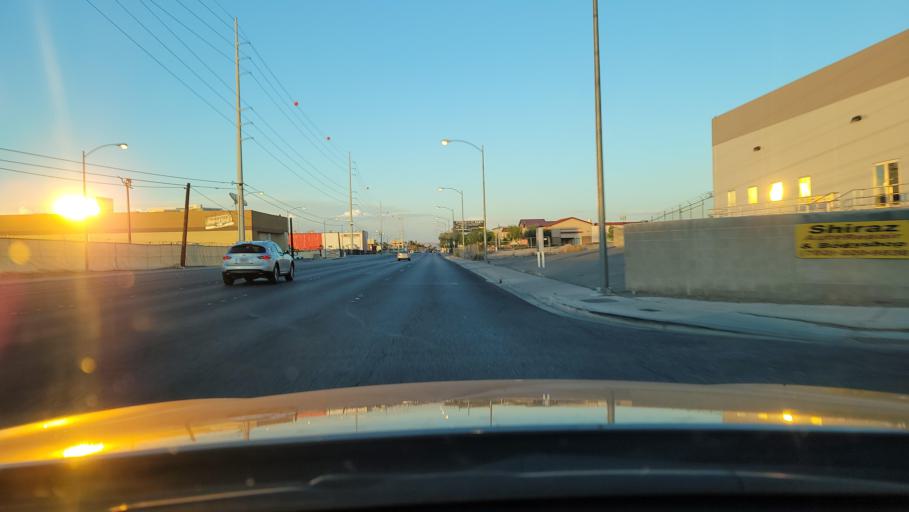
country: US
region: Nevada
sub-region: Clark County
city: Paradise
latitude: 36.0862
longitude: -115.1946
